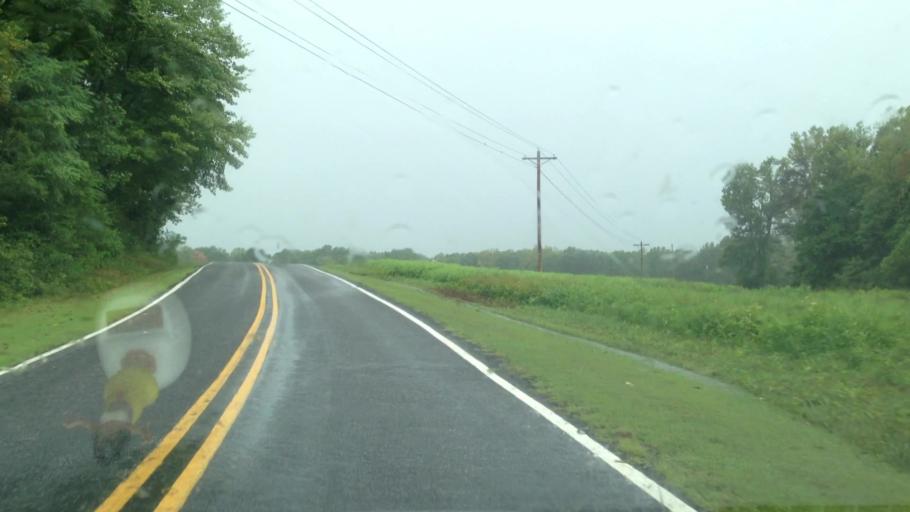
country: US
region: North Carolina
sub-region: Rockingham County
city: Mayodan
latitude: 36.4357
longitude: -80.0867
